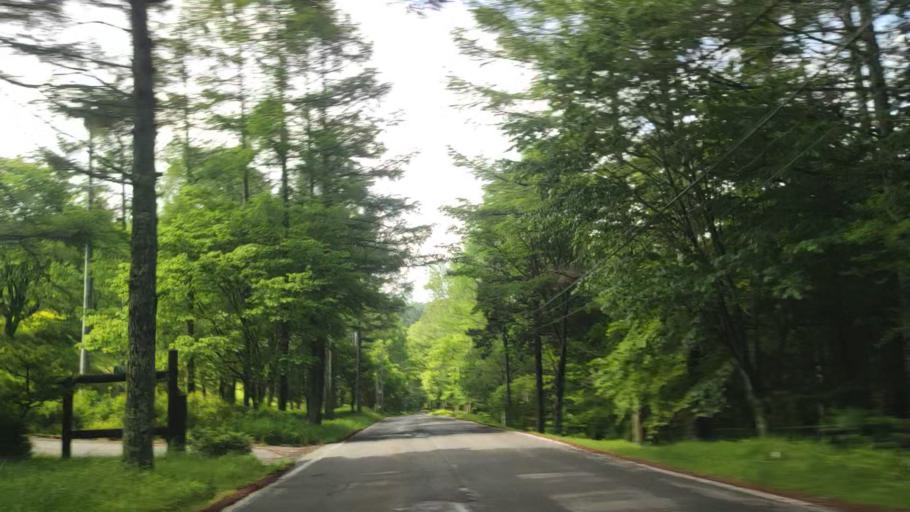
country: JP
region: Nagano
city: Suwa
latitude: 36.0880
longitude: 138.1437
